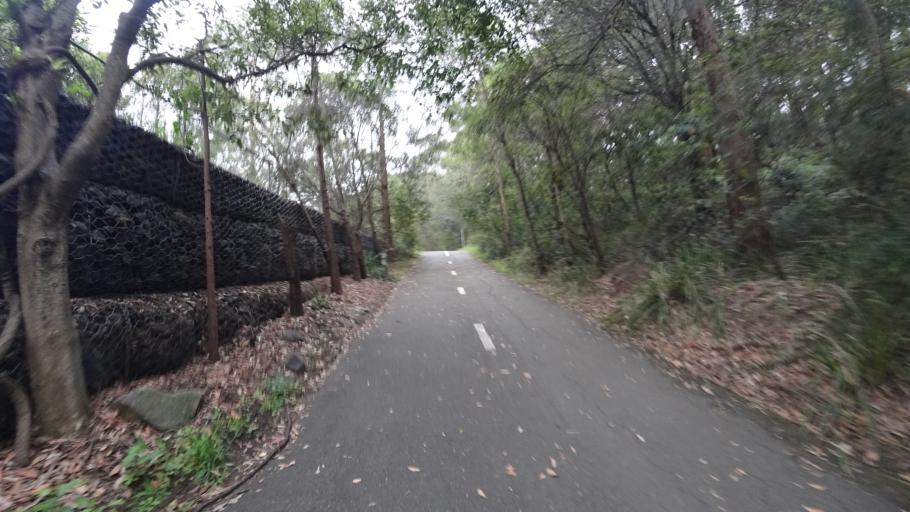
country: AU
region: New South Wales
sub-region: Willoughby
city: Artarmon
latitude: -33.8116
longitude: 151.1937
